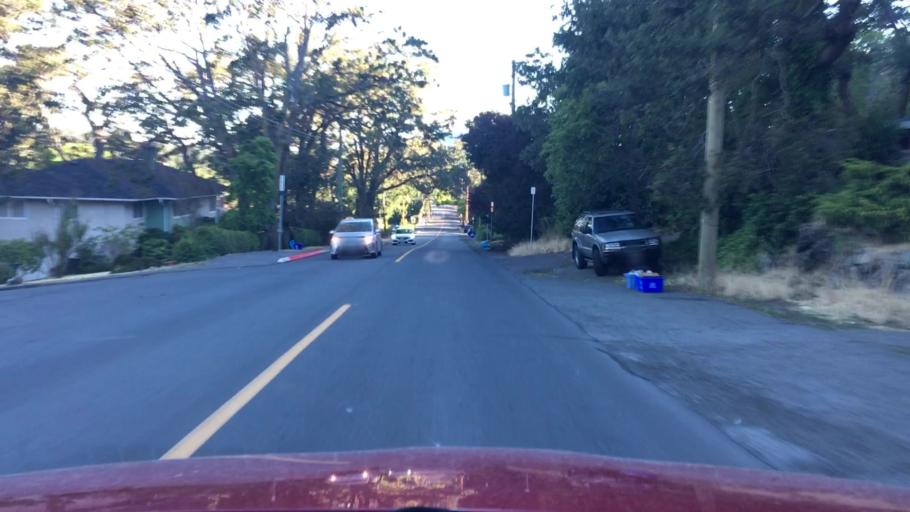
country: CA
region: British Columbia
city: Oak Bay
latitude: 48.4559
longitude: -123.3281
